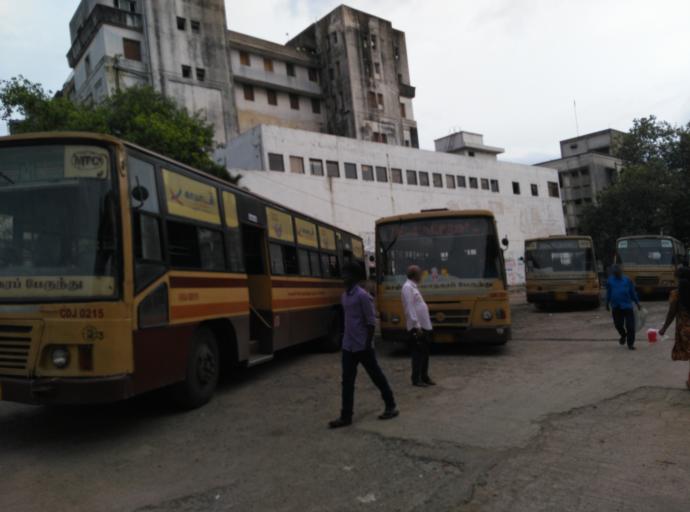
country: IN
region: Tamil Nadu
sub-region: Chennai
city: Chennai
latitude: 13.0872
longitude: 80.2839
